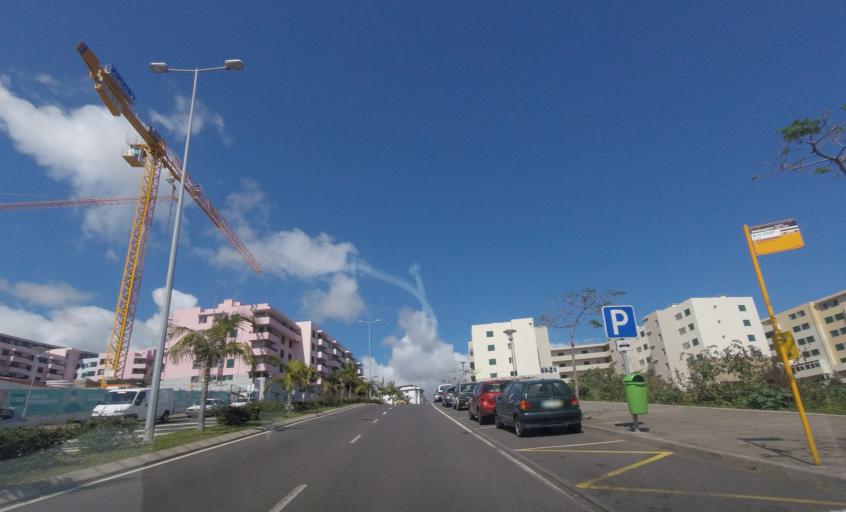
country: PT
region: Madeira
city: Camara de Lobos
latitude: 32.6469
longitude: -16.9417
